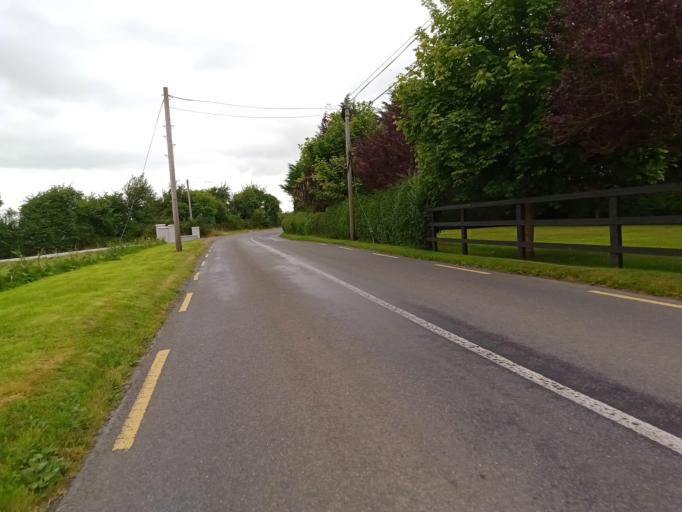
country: IE
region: Leinster
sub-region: Kilkenny
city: Callan
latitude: 52.5679
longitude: -7.4149
